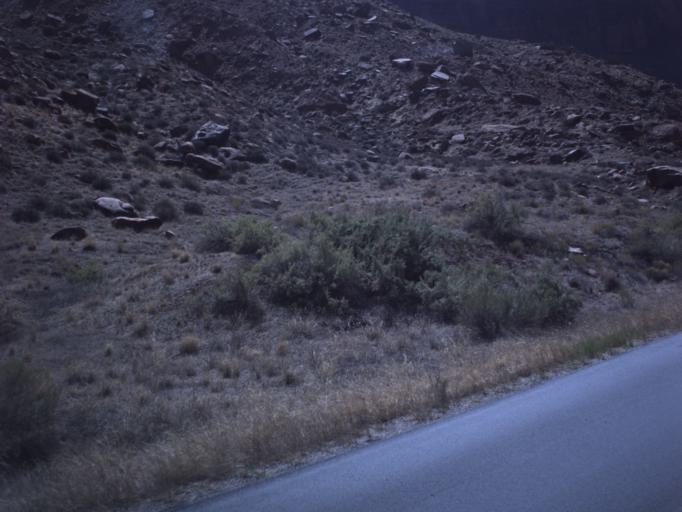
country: US
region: Utah
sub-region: Grand County
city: Moab
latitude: 38.6357
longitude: -109.4816
